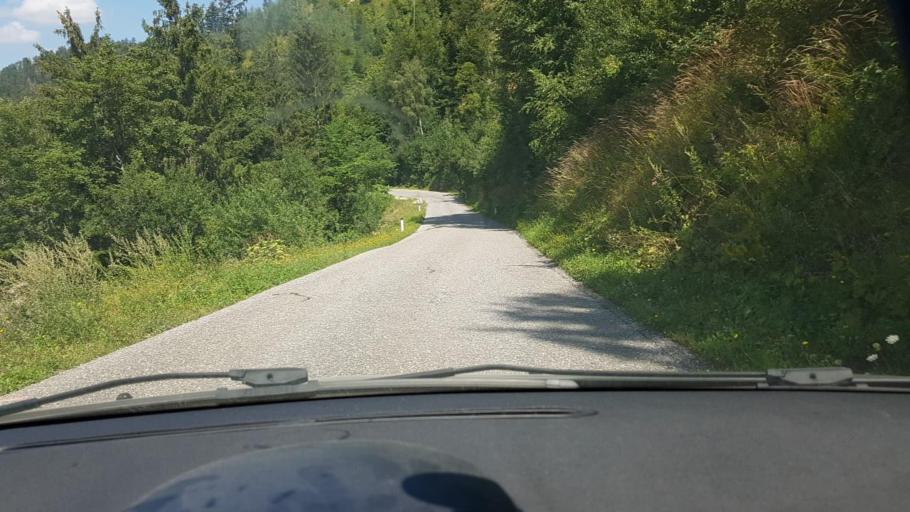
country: SI
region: Jezersko
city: Zgornje Jezersko
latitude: 46.4145
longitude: 14.5606
